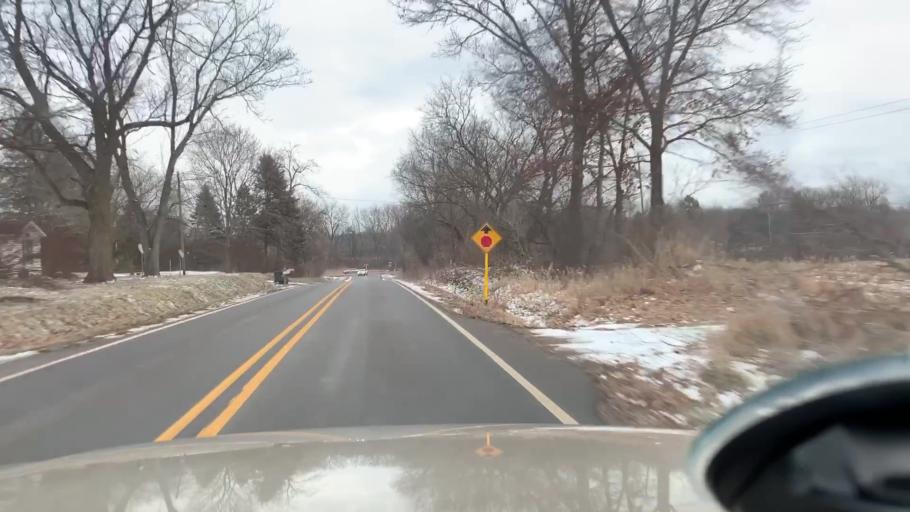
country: US
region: Michigan
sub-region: Jackson County
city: Spring Arbor
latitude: 42.2002
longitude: -84.5235
